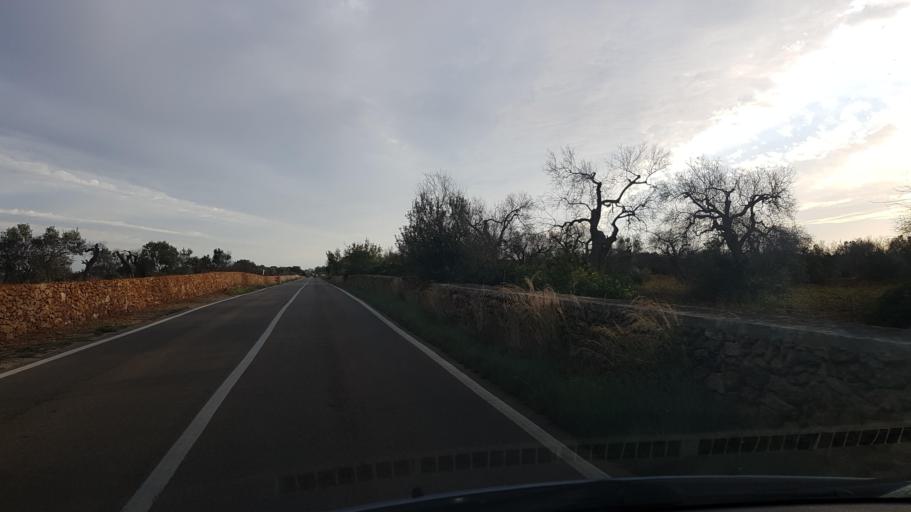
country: IT
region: Apulia
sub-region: Provincia di Brindisi
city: Torchiarolo
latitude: 40.4689
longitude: 18.1194
